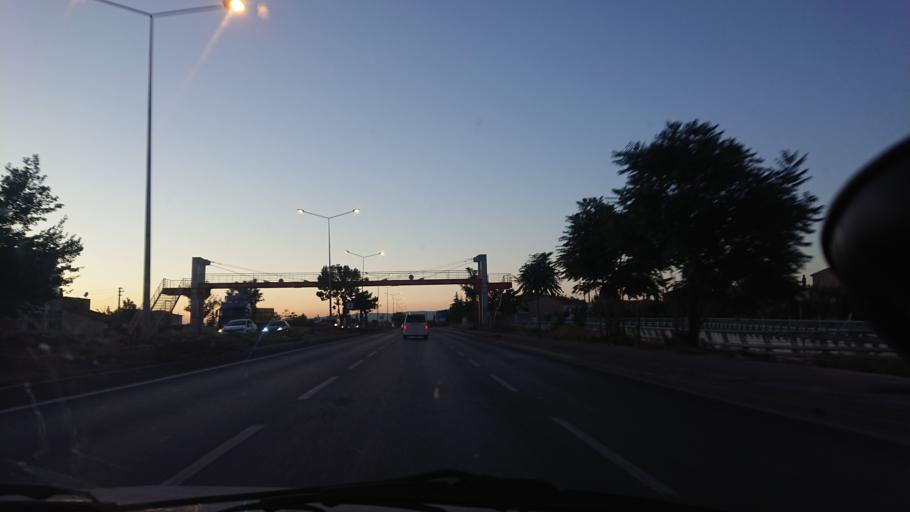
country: TR
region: Eskisehir
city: Eskisehir
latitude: 39.7669
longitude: 30.5643
